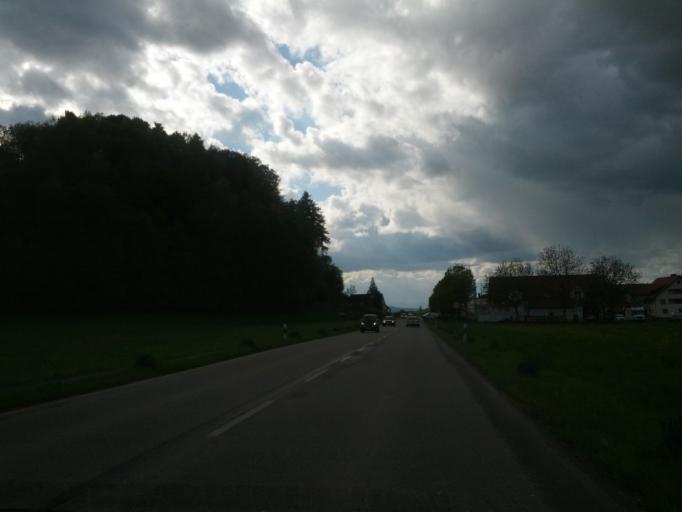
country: DE
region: Baden-Wuerttemberg
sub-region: Freiburg Region
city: Heuweiler
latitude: 48.0530
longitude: 7.9255
